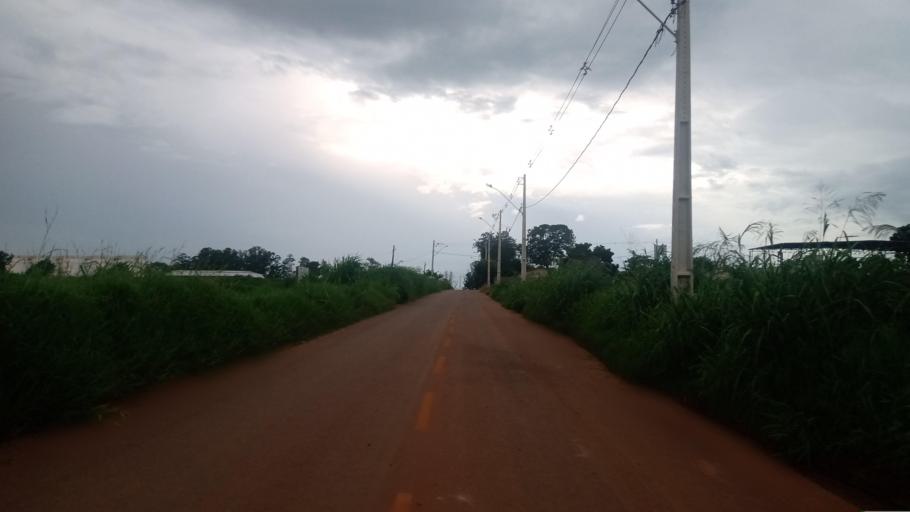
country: BR
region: Goias
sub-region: Senador Canedo
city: Senador Canedo
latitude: -16.7184
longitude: -49.1182
